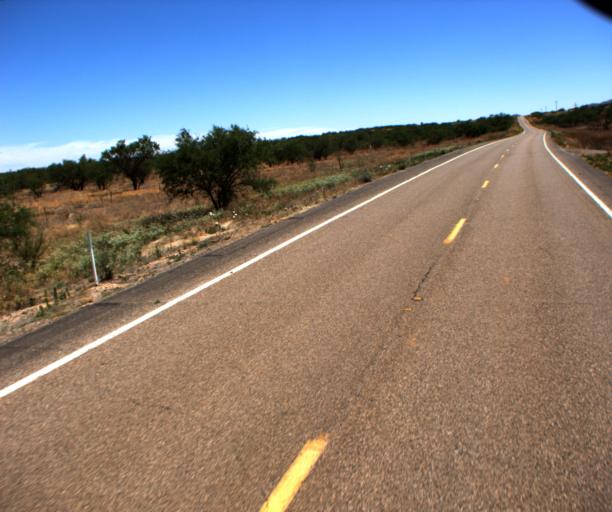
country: US
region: Arizona
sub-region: Pima County
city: Sells
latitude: 31.6022
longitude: -111.5240
